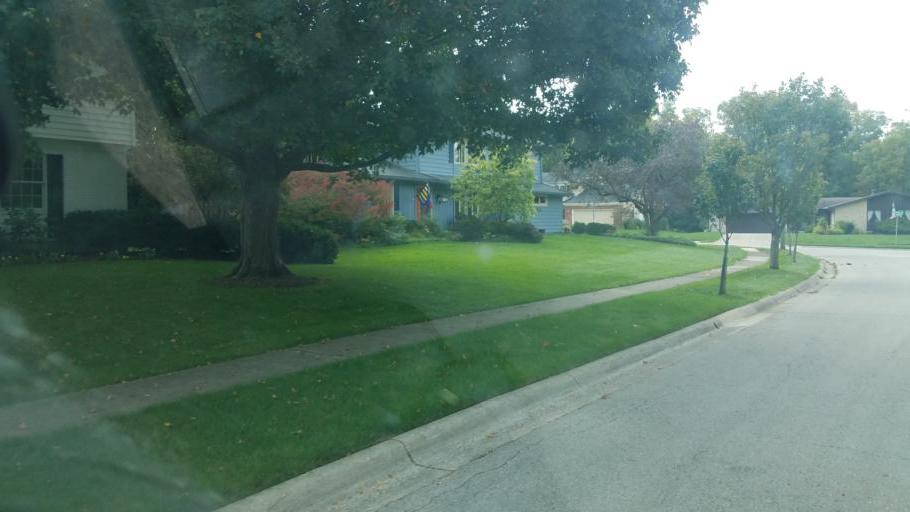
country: US
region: Ohio
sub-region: Franklin County
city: Worthington
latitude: 40.1084
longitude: -83.0279
